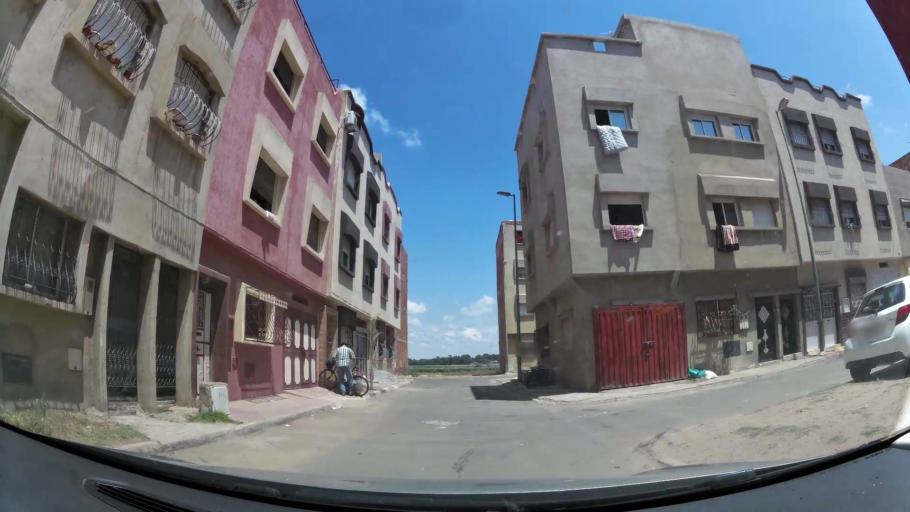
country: MA
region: Gharb-Chrarda-Beni Hssen
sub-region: Kenitra Province
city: Kenitra
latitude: 34.2653
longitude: -6.5537
